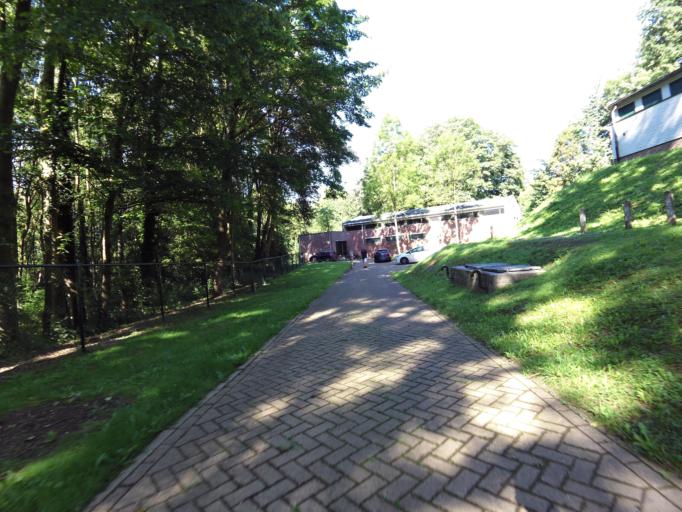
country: NL
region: Limburg
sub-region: Gemeente Voerendaal
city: Ubachsberg
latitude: 50.8266
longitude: 5.9174
